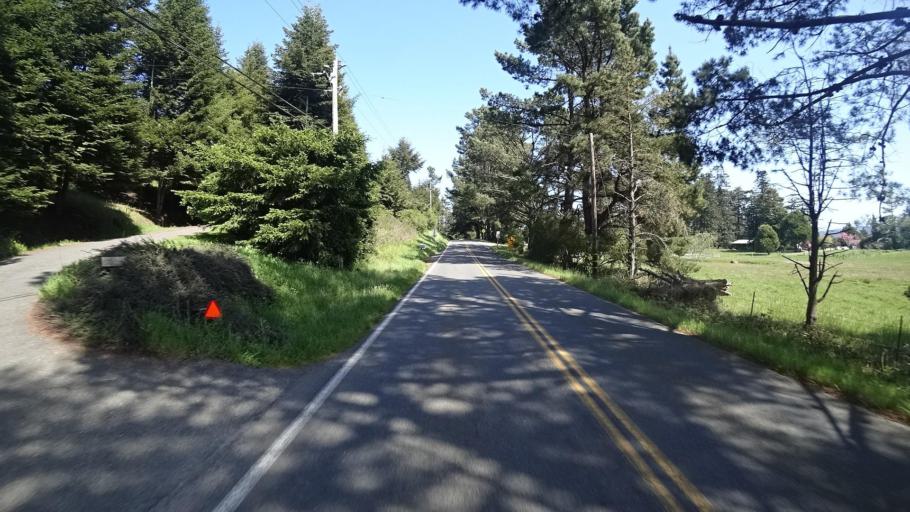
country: US
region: California
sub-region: Humboldt County
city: Hydesville
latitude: 40.5519
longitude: -124.1150
